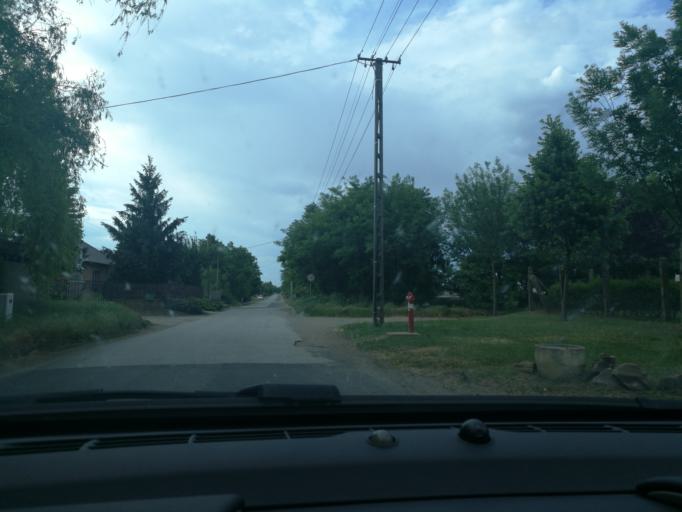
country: HU
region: Szabolcs-Szatmar-Bereg
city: Nyirpazony
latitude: 47.9367
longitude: 21.7964
